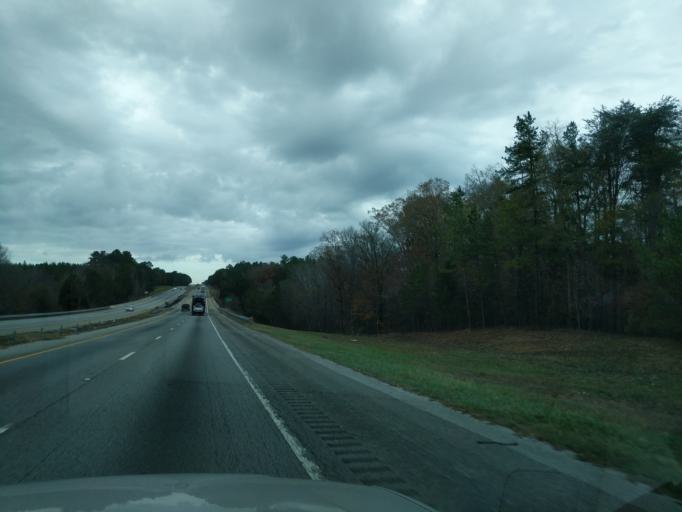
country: US
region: South Carolina
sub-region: Spartanburg County
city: Woodruff
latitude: 34.7620
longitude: -81.9539
